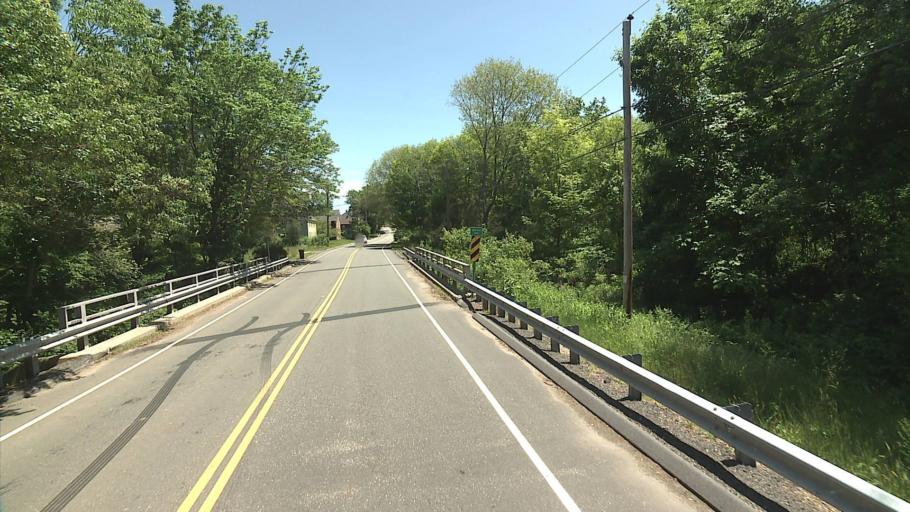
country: US
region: Rhode Island
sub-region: Washington County
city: Hopkinton
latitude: 41.4561
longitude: -71.8168
